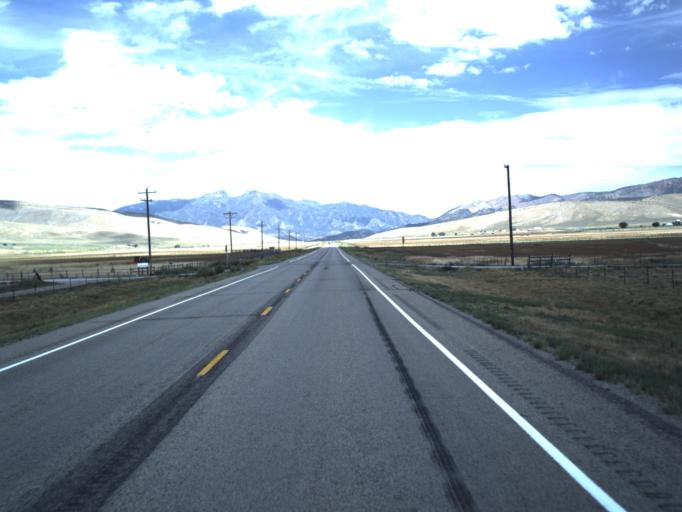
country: US
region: Utah
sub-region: Sanpete County
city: Fairview
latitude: 39.7789
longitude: -111.4912
